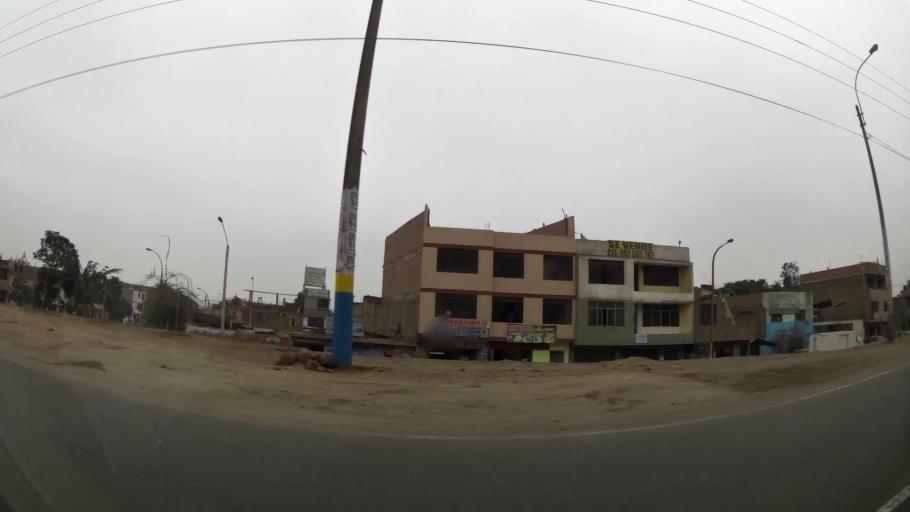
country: PE
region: Lima
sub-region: Lima
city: Urb. Santo Domingo
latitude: -11.9096
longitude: -77.0373
